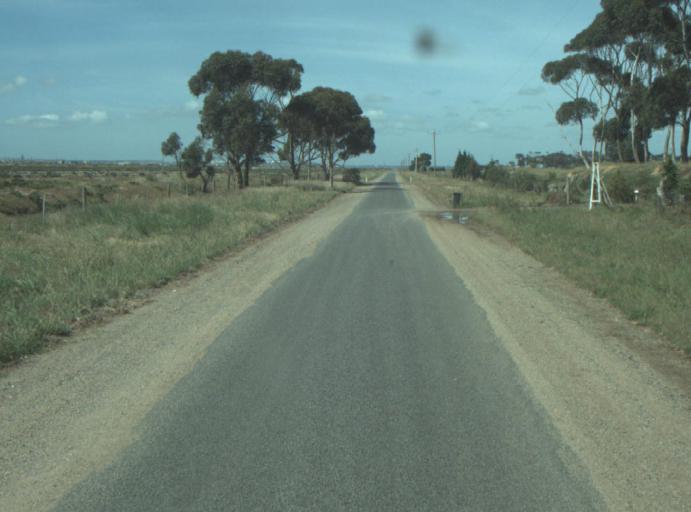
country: AU
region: Victoria
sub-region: Greater Geelong
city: Lara
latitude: -38.0704
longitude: 144.4249
